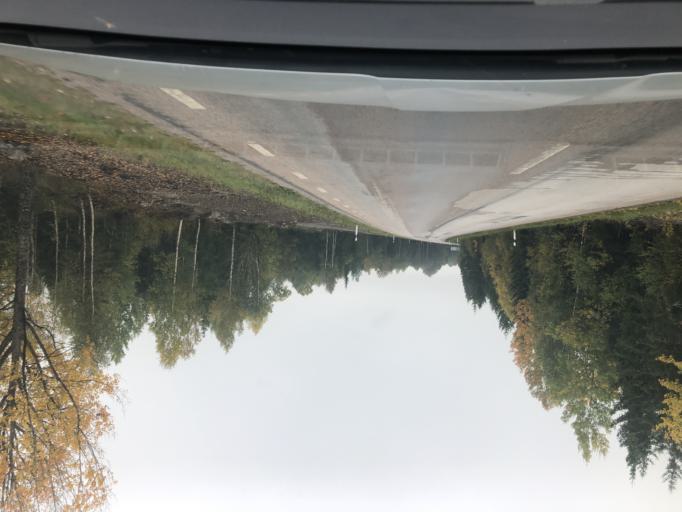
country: SE
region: Uppsala
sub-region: Tierps Kommun
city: Orbyhus
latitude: 60.2163
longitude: 17.7039
